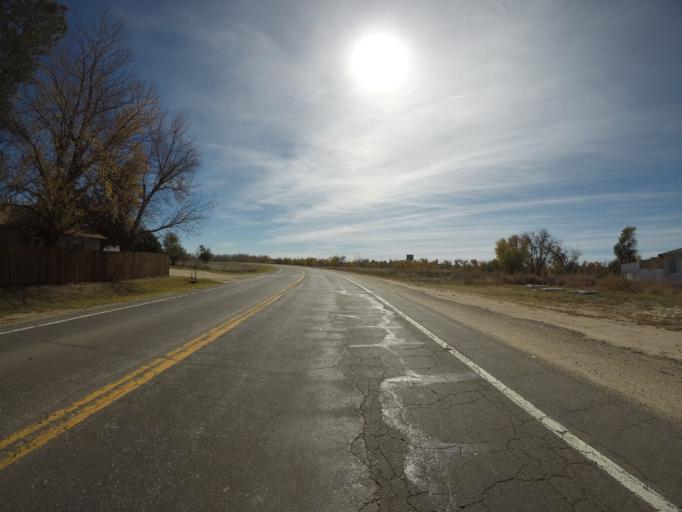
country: US
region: Colorado
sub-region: Yuma County
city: Yuma
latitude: 39.6619
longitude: -102.8511
